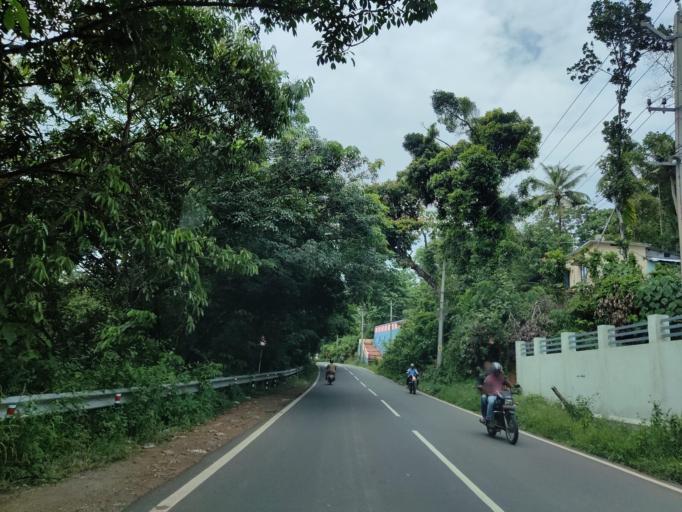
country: IN
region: Kerala
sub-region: Alappuzha
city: Chengannur
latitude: 9.2763
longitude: 76.6146
